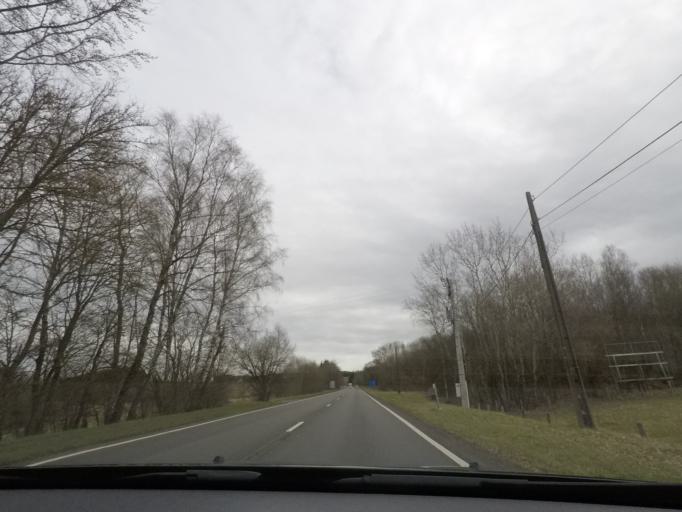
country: BE
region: Wallonia
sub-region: Province du Luxembourg
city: Bastogne
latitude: 49.9792
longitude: 5.7738
